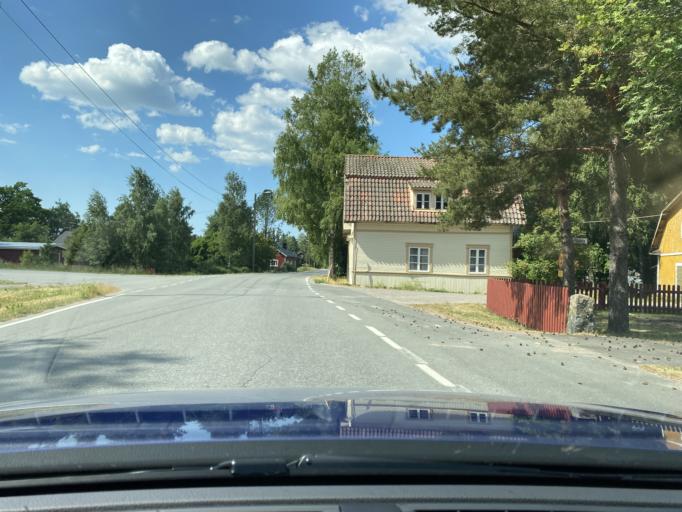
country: FI
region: Satakunta
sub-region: Rauma
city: Eura
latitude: 61.1411
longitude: 22.1211
